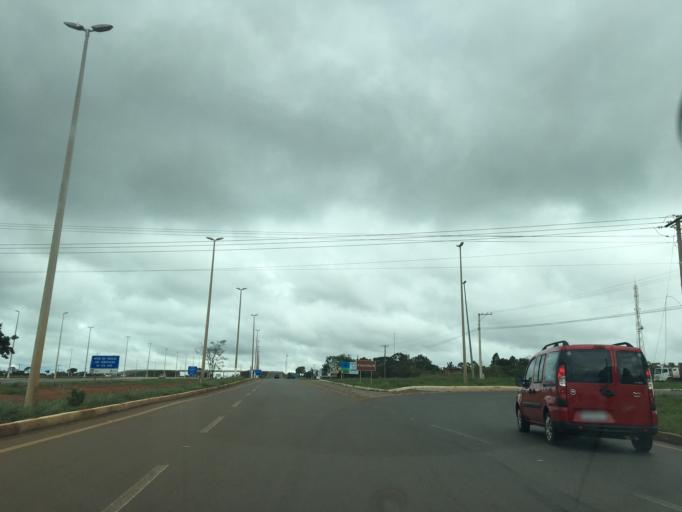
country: BR
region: Federal District
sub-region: Brasilia
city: Brasilia
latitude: -15.9760
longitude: -47.9906
